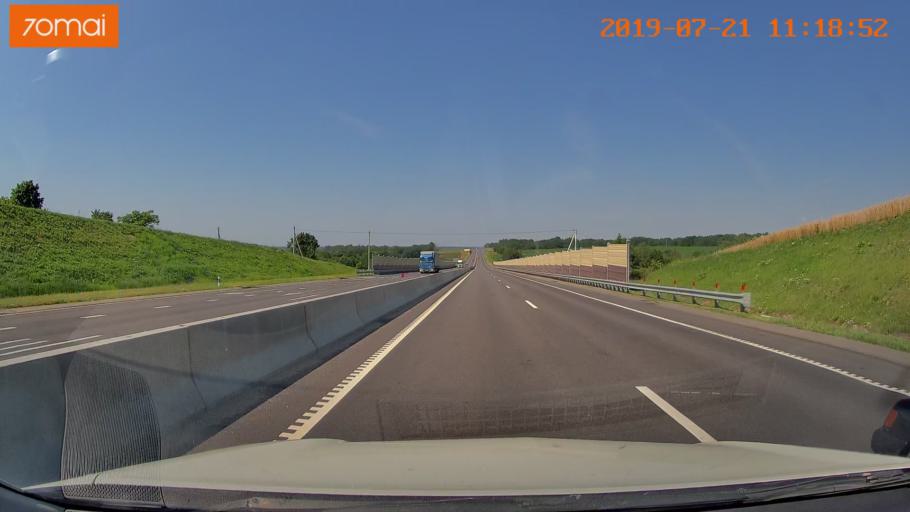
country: BY
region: Minsk
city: Ivyanyets
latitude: 54.0411
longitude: 26.6900
